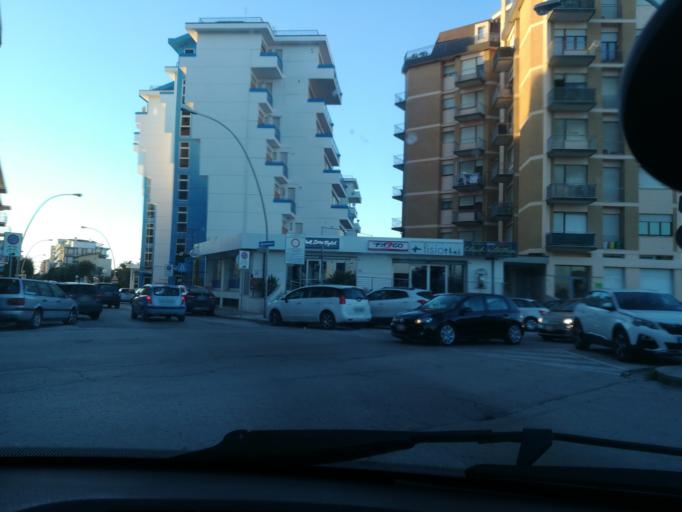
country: IT
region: The Marches
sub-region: Provincia di Macerata
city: Portocivitanova
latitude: 43.3001
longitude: 13.7378
